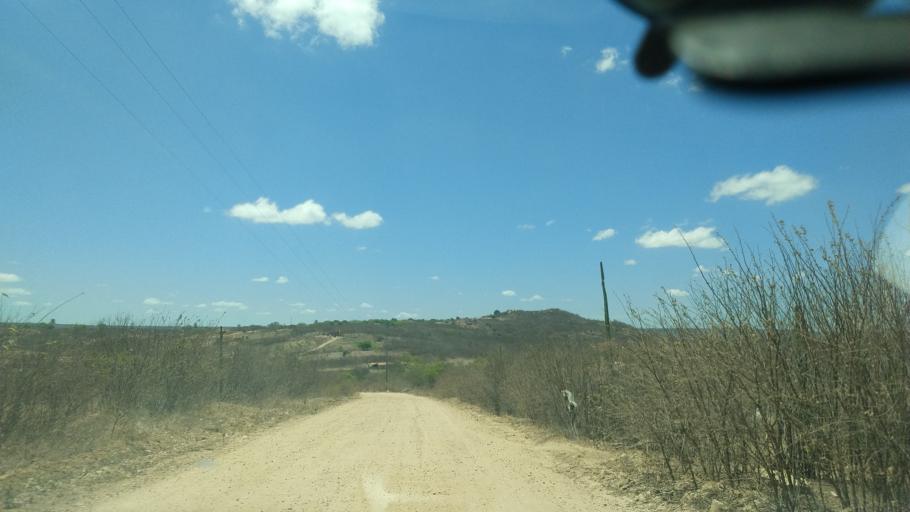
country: BR
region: Rio Grande do Norte
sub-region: Cerro Cora
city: Cerro Cora
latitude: -6.0180
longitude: -36.3302
